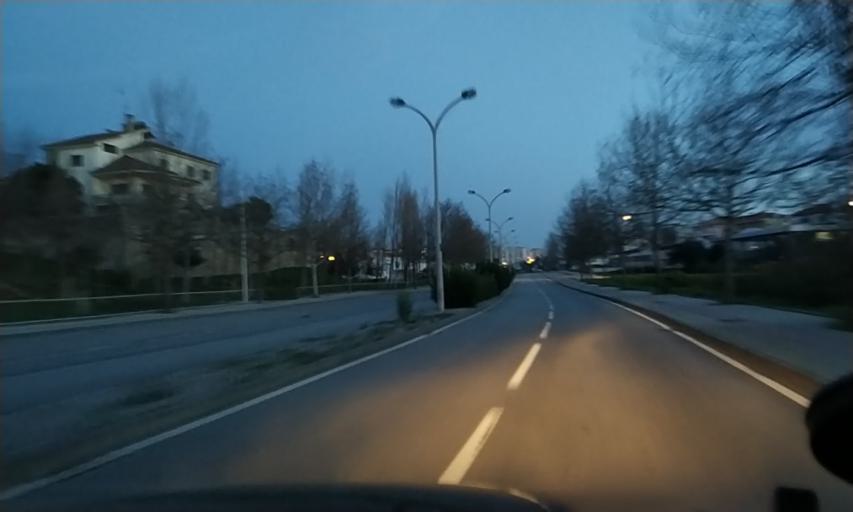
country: PT
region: Castelo Branco
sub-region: Castelo Branco
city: Castelo Branco
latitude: 39.8234
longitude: -7.5096
